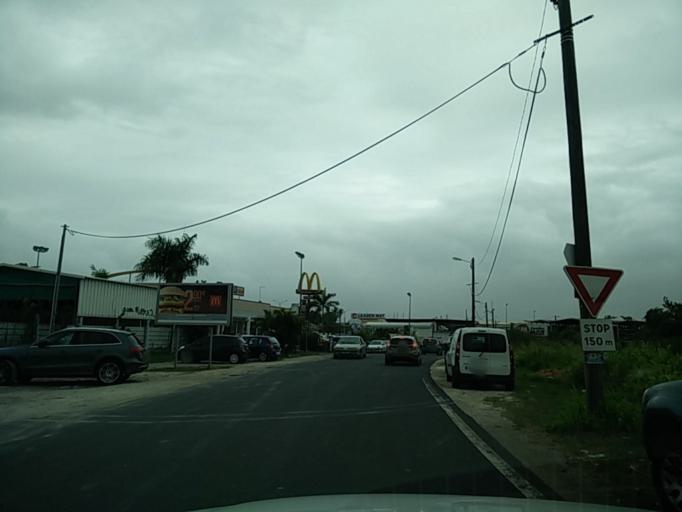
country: GP
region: Guadeloupe
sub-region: Guadeloupe
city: Baie-Mahault
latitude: 16.2535
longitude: -61.5624
